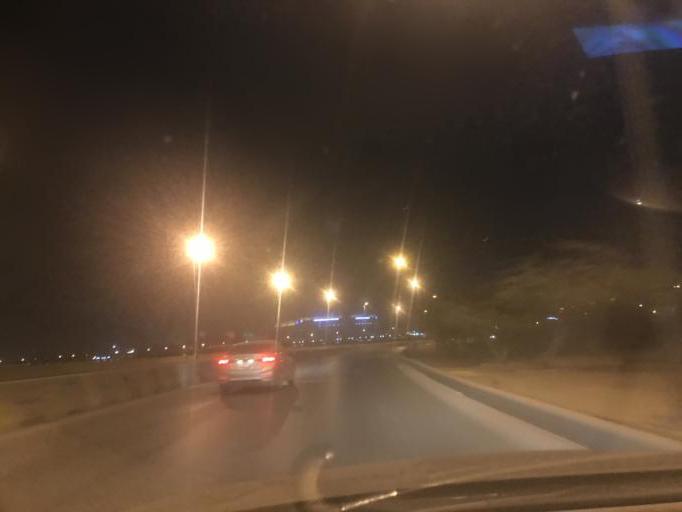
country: SA
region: Ar Riyad
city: Riyadh
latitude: 24.8275
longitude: 46.7170
